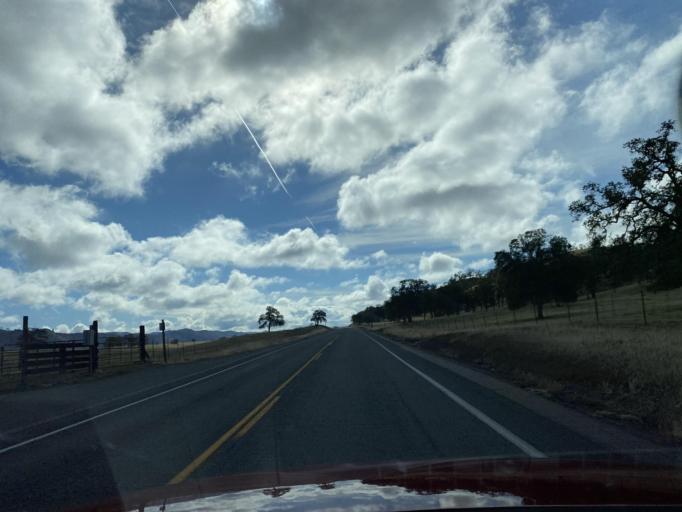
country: US
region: California
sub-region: Glenn County
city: Willows
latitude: 39.5379
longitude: -122.5350
